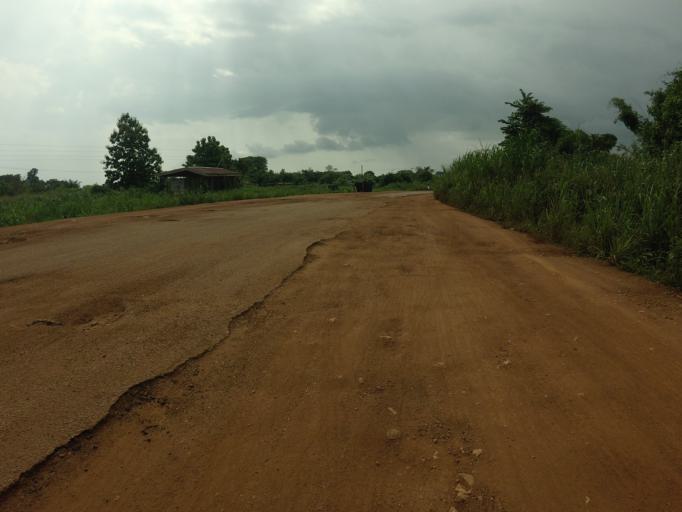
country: GH
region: Volta
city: Kpandu
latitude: 6.9904
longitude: 0.4404
